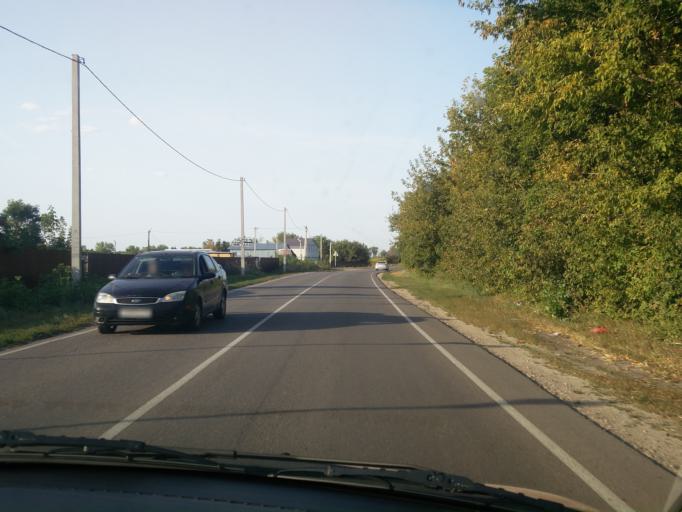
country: RU
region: Voronezj
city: Ramon'
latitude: 51.9181
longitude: 39.3205
